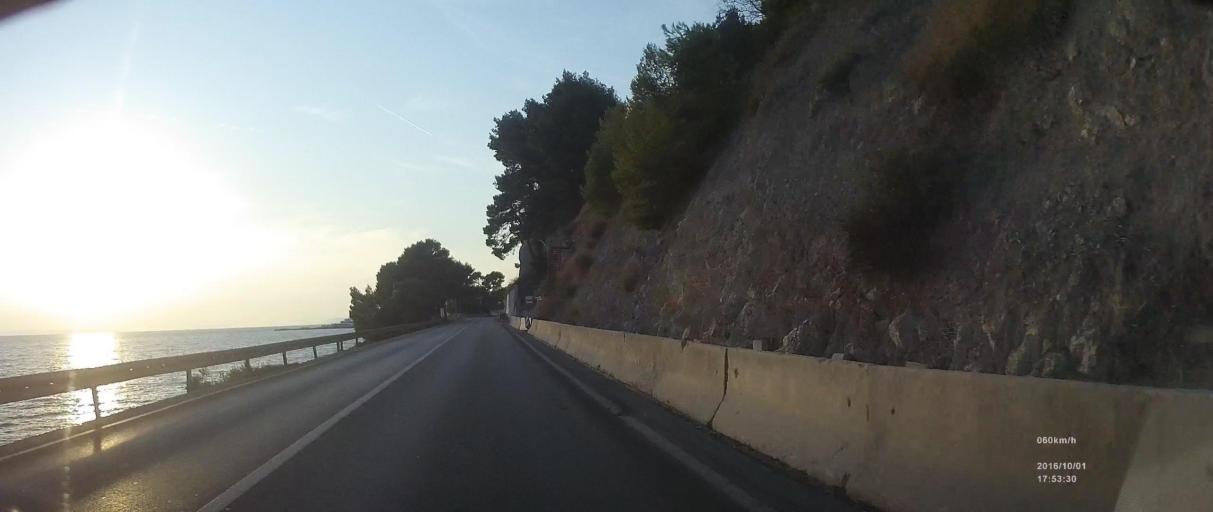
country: HR
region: Splitsko-Dalmatinska
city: Jesenice
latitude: 43.4582
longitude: 16.6090
